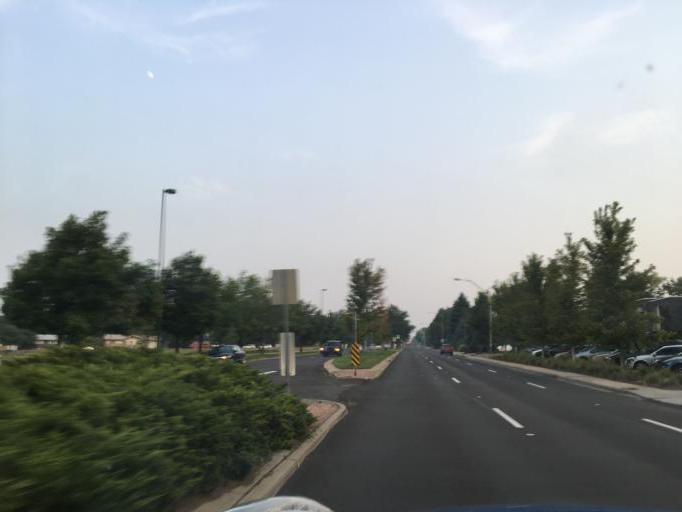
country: US
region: Colorado
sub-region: Arapahoe County
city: Glendale
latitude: 39.6743
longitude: -104.9129
